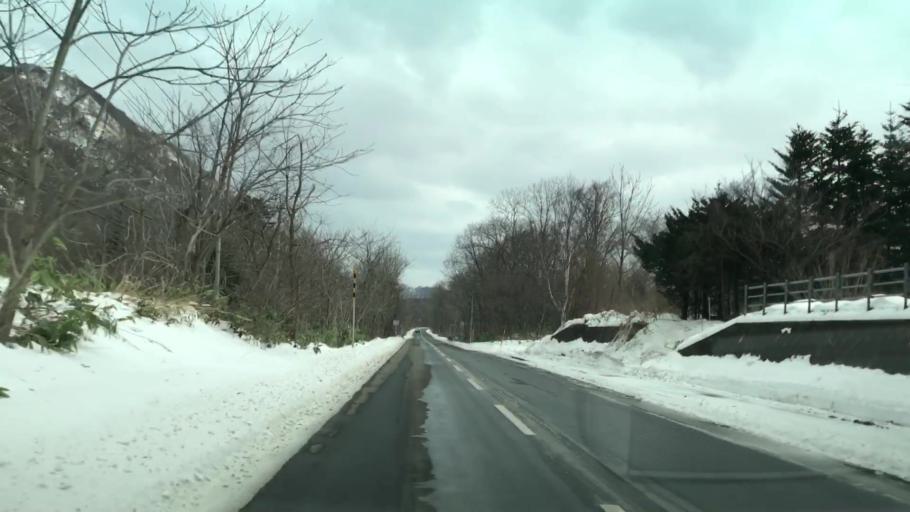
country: JP
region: Hokkaido
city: Yoichi
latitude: 43.3312
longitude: 140.4713
